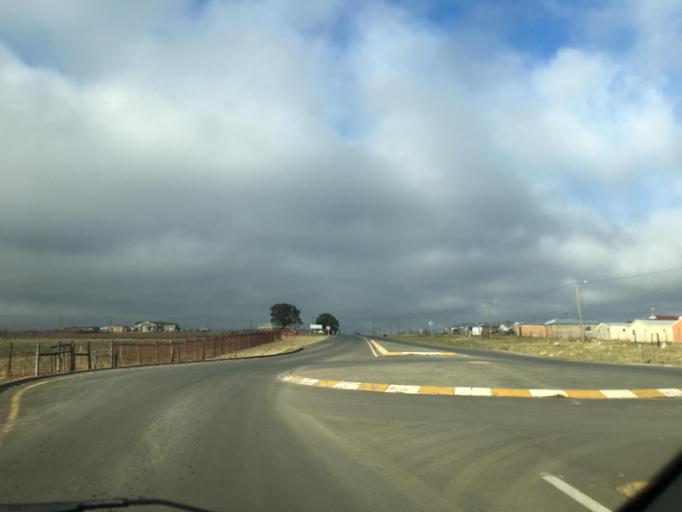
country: ZA
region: Eastern Cape
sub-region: Chris Hani District Municipality
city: Elliot
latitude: -31.3389
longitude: 27.8381
